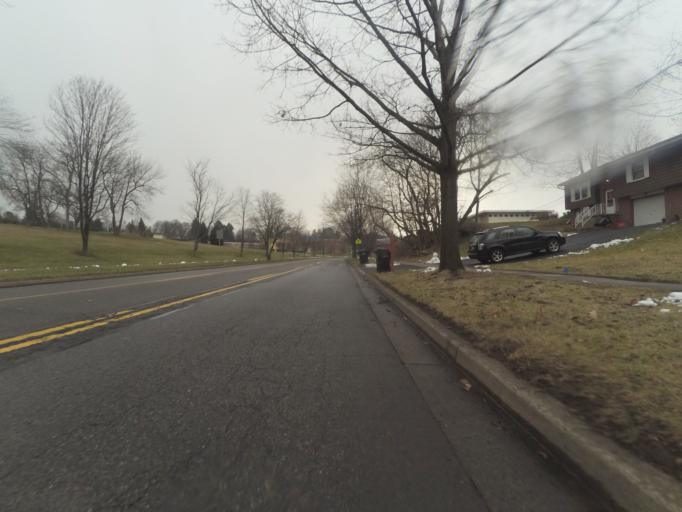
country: US
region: Pennsylvania
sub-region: Centre County
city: State College
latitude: 40.7909
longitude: -77.8472
